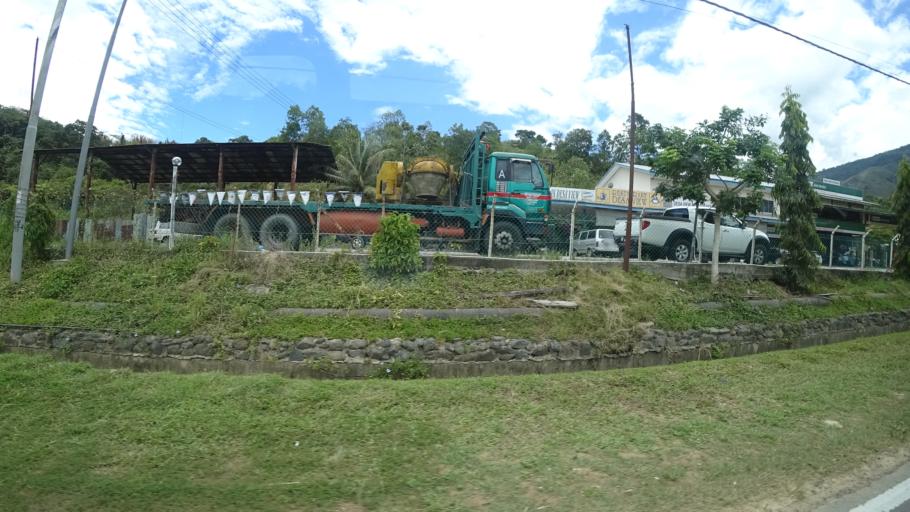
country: MY
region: Sabah
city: Ranau
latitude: 5.9734
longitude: 116.6798
